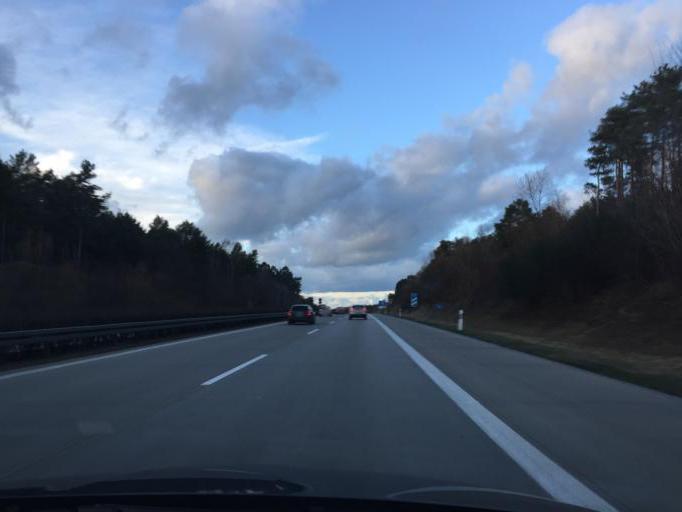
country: DE
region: Brandenburg
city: Schwerin
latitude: 52.2035
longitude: 13.6119
